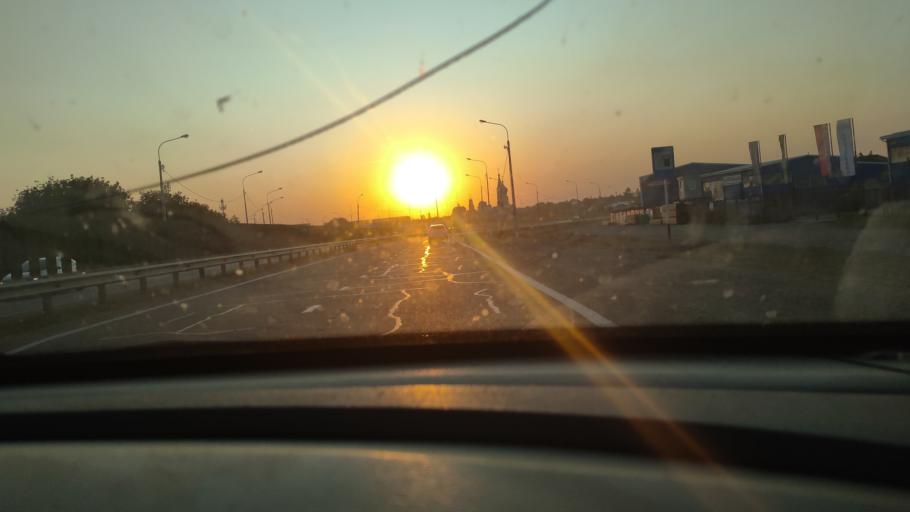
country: RU
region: Krasnodarskiy
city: Timashevsk
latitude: 45.6011
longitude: 38.9634
